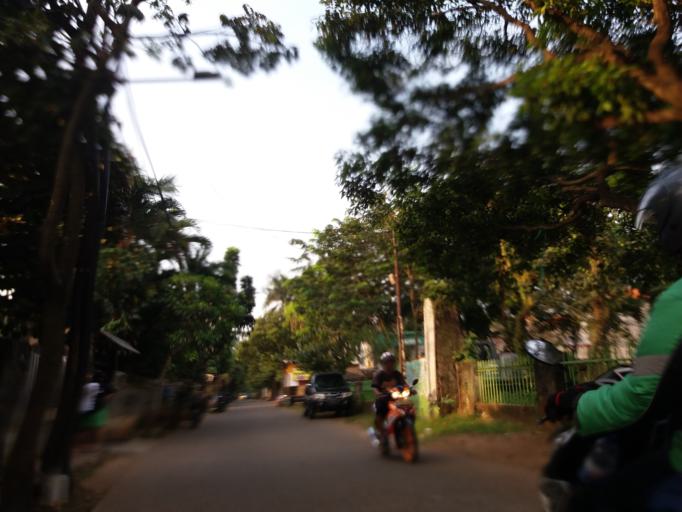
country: ID
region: Jakarta Raya
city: Jakarta
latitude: -6.2428
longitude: 106.8146
